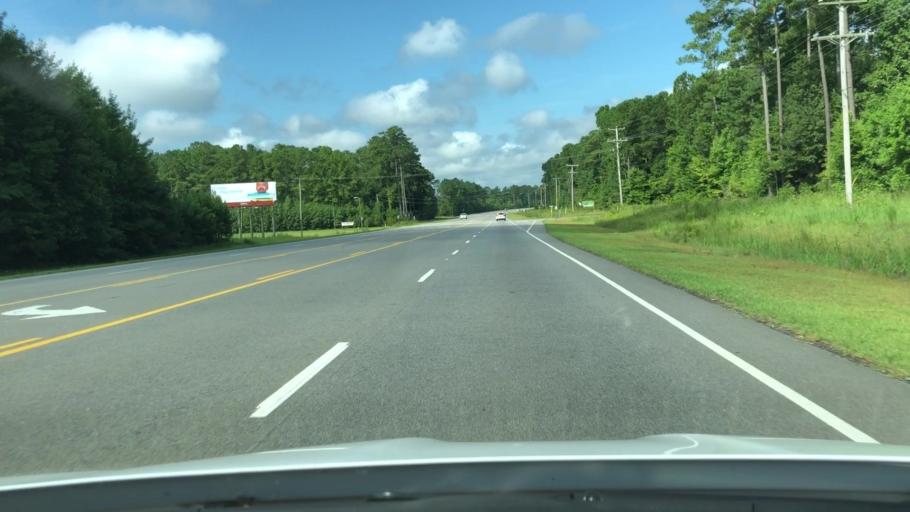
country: US
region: North Carolina
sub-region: Bertie County
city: Windsor
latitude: 36.0199
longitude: -76.8268
